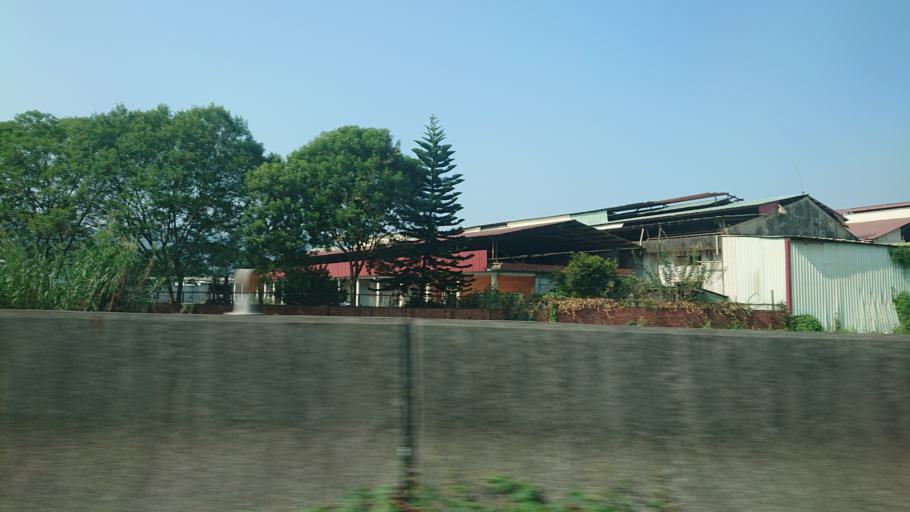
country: TW
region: Taiwan
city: Lugu
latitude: 23.7658
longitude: 120.6597
